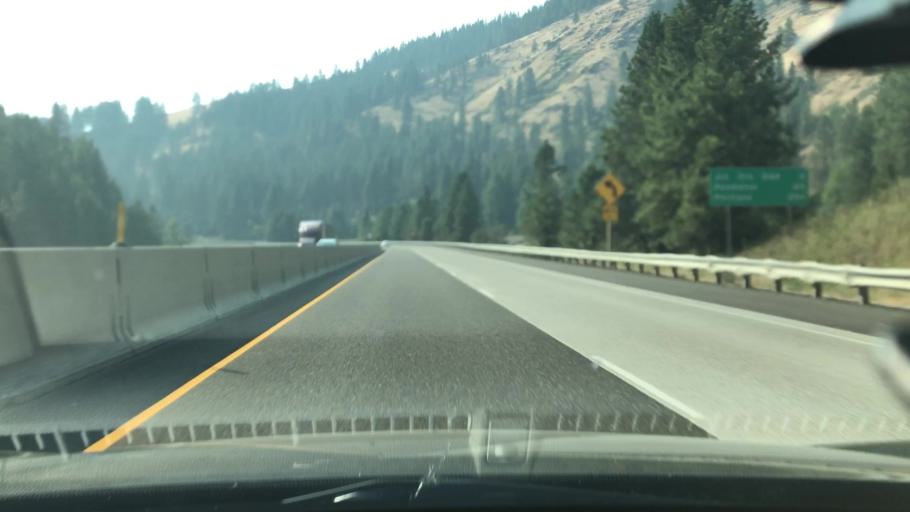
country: US
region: Oregon
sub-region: Union County
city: La Grande
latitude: 45.3536
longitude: -118.1847
